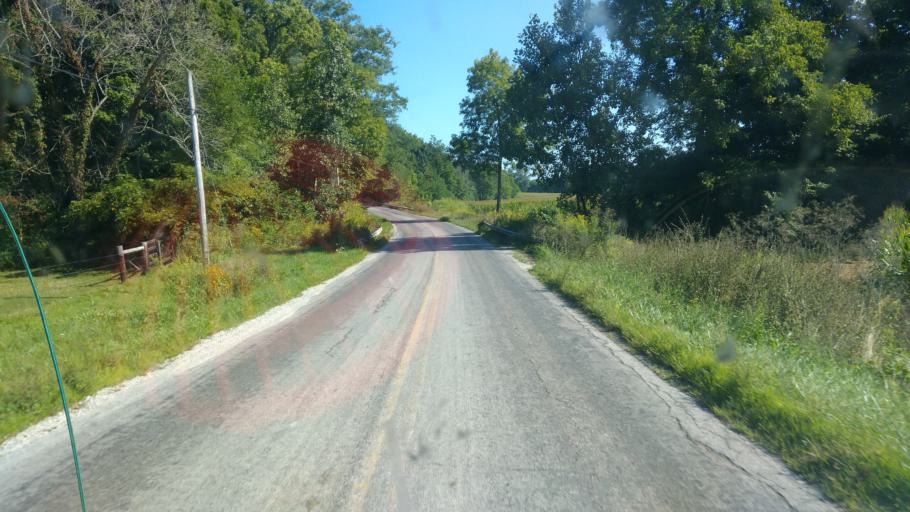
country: US
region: Ohio
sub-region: Ashland County
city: Ashland
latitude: 40.8972
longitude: -82.4326
